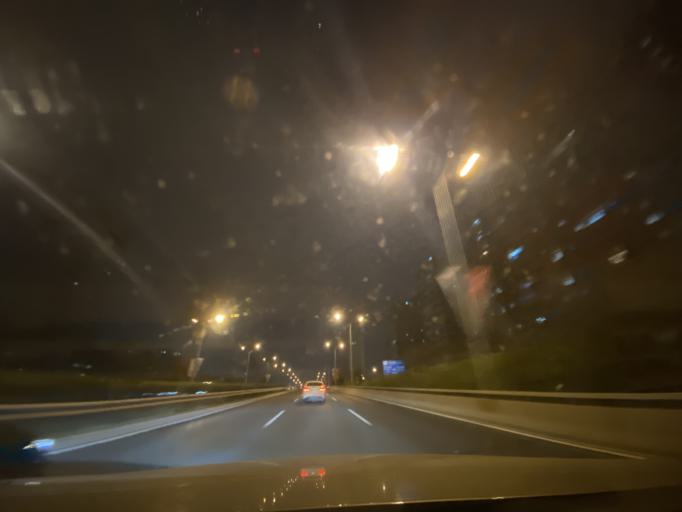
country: CN
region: Beijing
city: Lugouqiao
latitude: 39.8958
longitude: 116.2920
